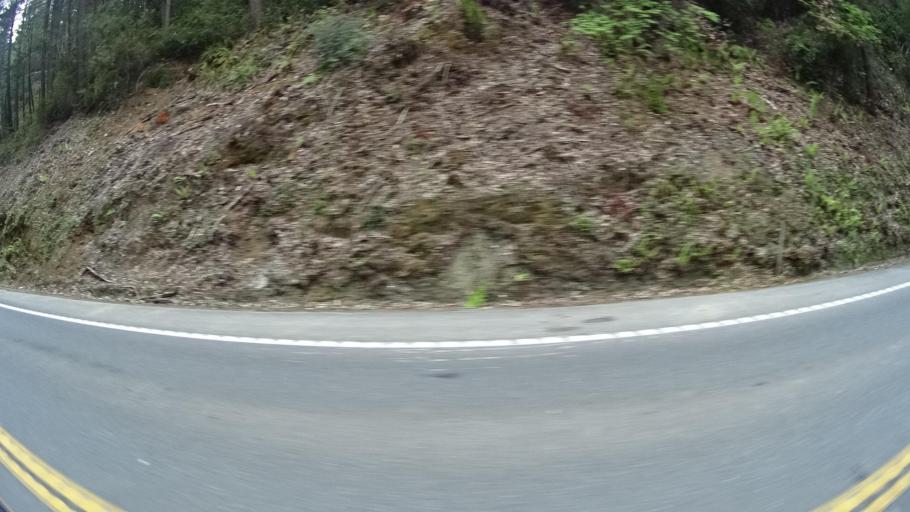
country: US
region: California
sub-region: Humboldt County
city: Willow Creek
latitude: 41.0030
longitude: -123.6489
